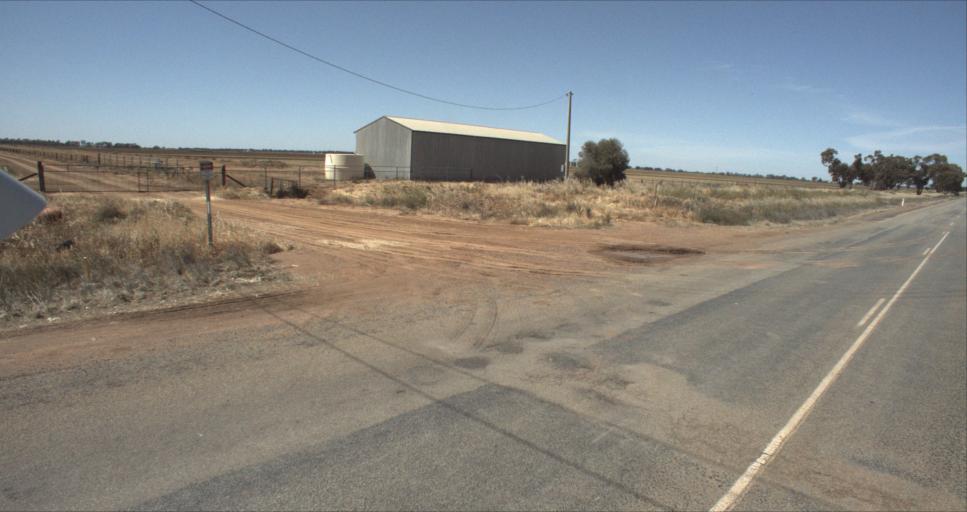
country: AU
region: New South Wales
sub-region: Leeton
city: Leeton
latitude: -34.4999
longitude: 146.2871
